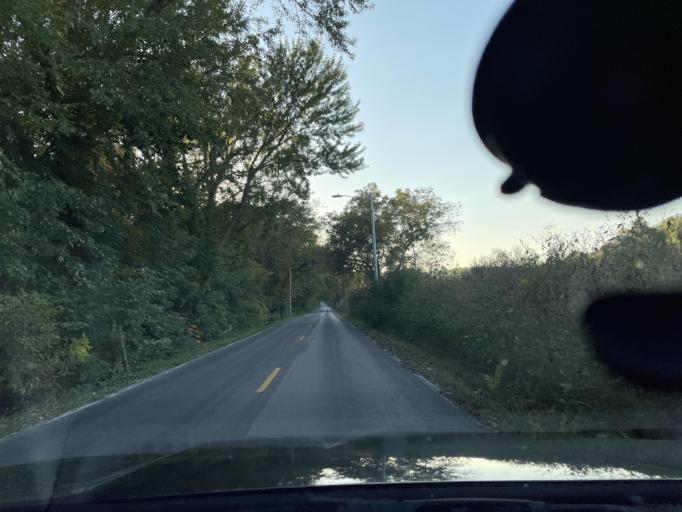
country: US
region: Missouri
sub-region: Buchanan County
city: Saint Joseph
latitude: 39.7994
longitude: -94.8331
